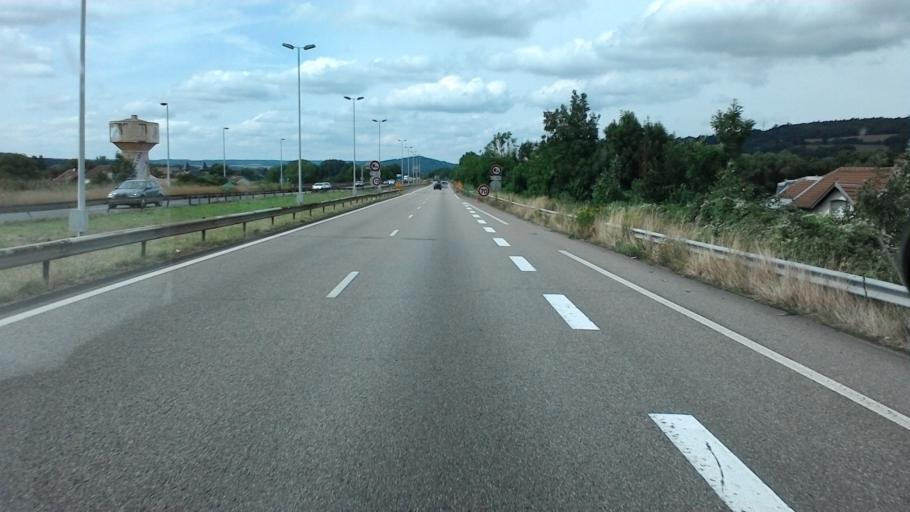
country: FR
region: Lorraine
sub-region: Departement de Meurthe-et-Moselle
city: Belleville
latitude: 48.8172
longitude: 6.1095
